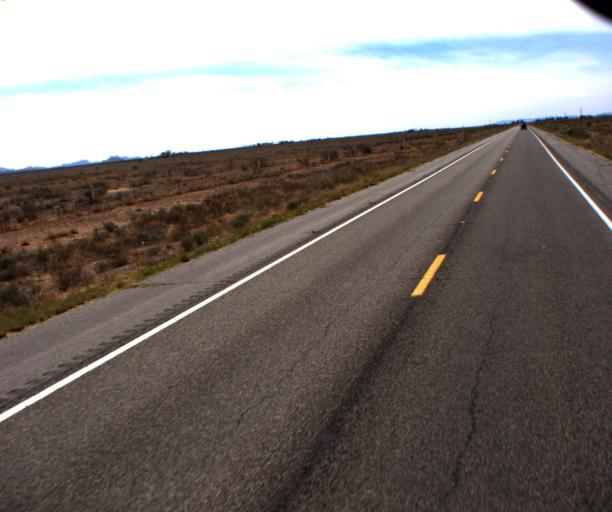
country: US
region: Arizona
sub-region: Cochise County
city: Pirtleville
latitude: 31.6273
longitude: -109.6716
